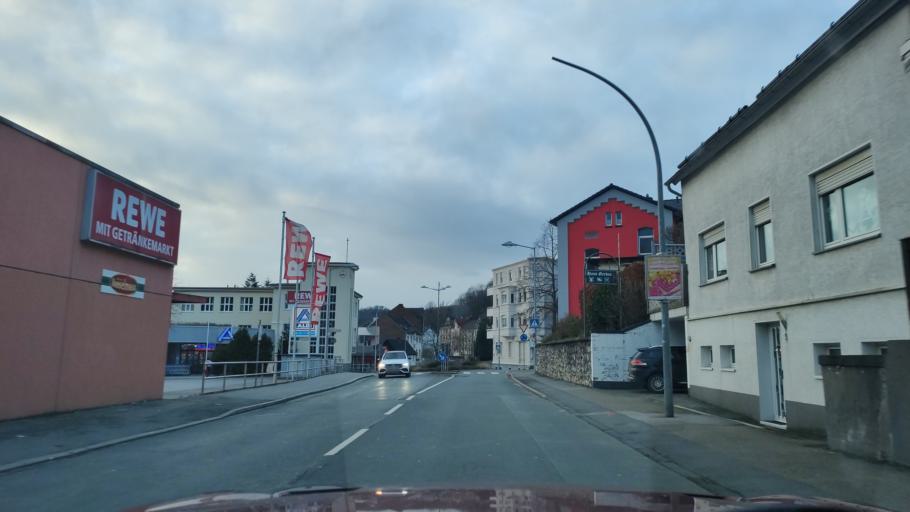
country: DE
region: North Rhine-Westphalia
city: Iserlohn
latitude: 51.3667
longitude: 7.6670
